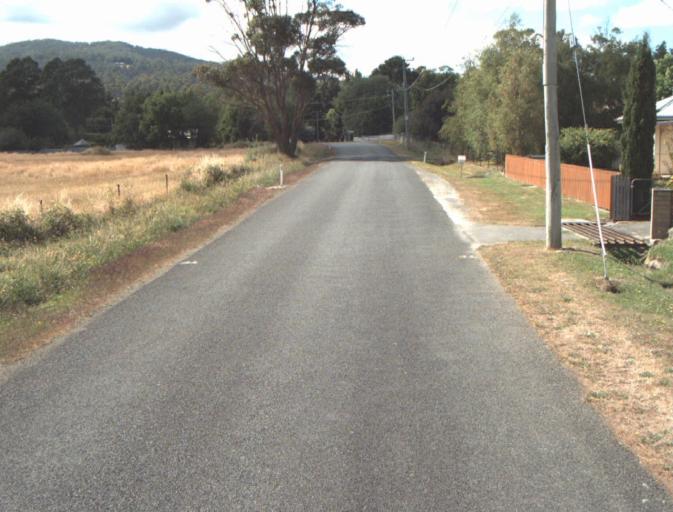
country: AU
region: Tasmania
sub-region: Launceston
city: Mayfield
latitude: -41.2604
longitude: 147.1569
